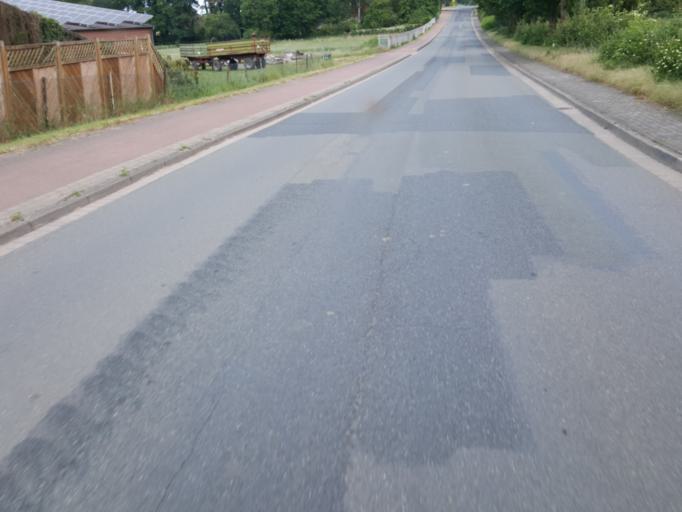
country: DE
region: Lower Saxony
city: Husum
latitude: 52.5671
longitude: 9.2505
